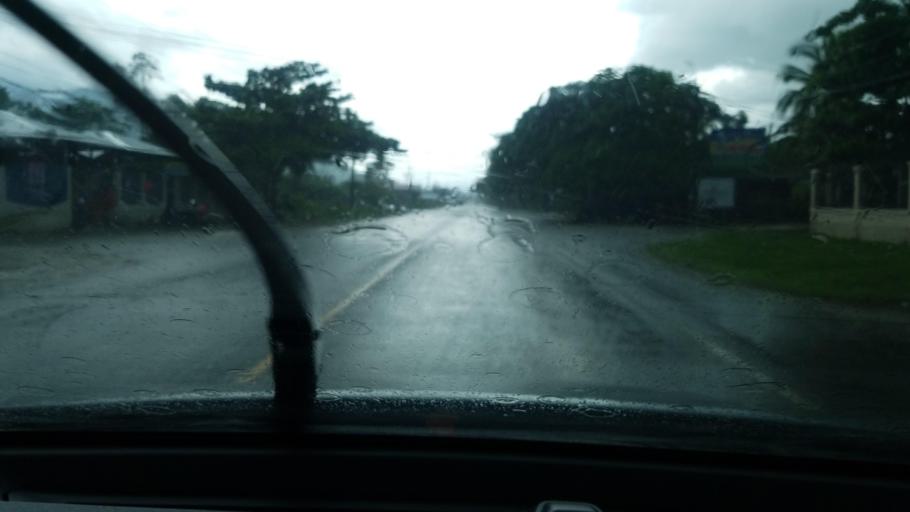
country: HN
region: Cortes
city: Rio Chiquito
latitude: 15.6271
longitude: -88.2557
